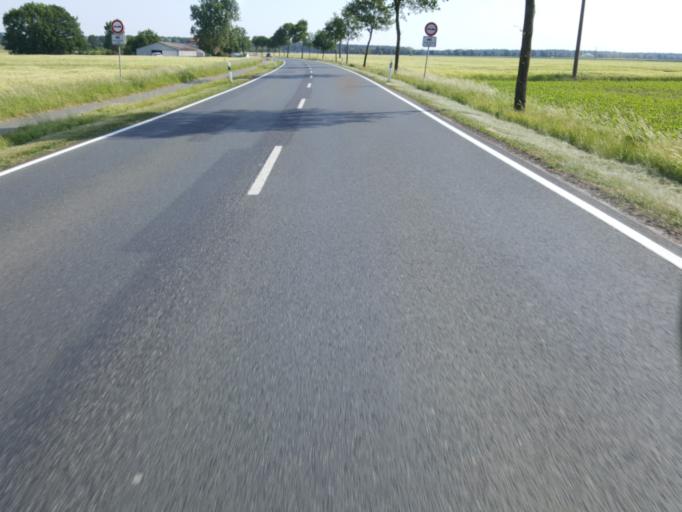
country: DE
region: Lower Saxony
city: Landesbergen
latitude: 52.5710
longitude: 9.1369
